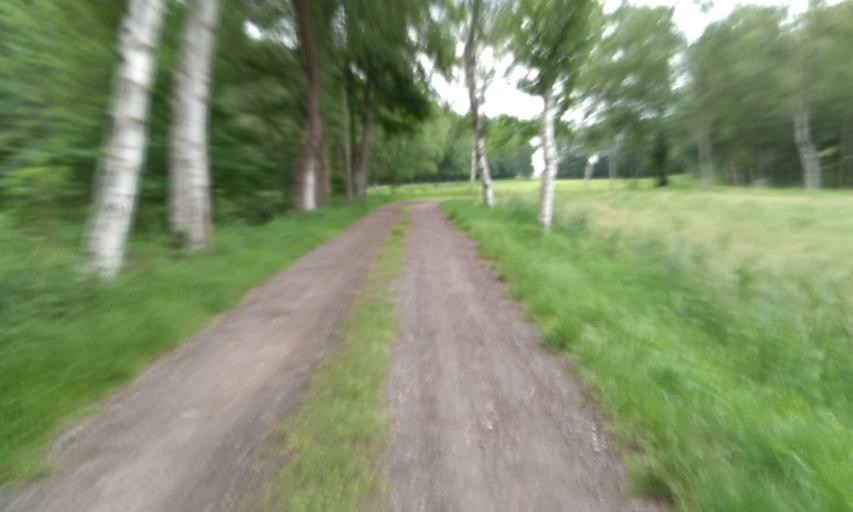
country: DE
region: Lower Saxony
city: Buxtehude
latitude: 53.4895
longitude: 9.6796
